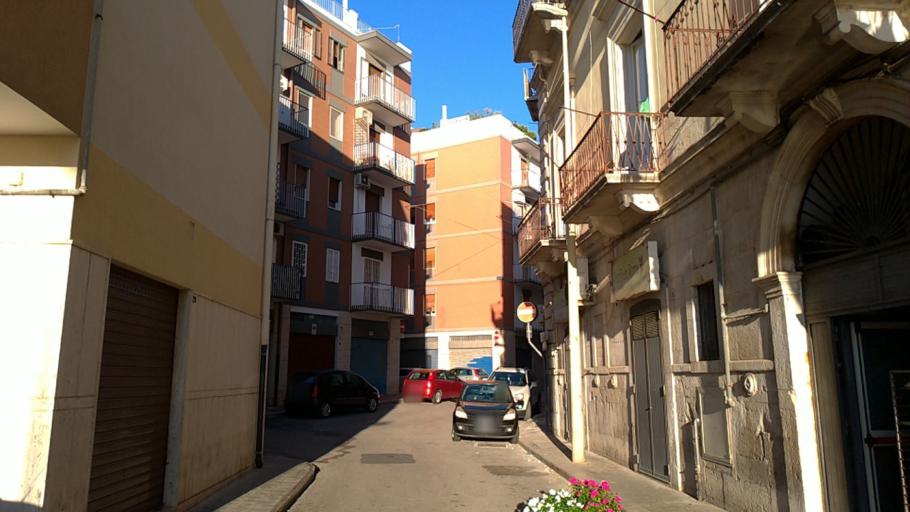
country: IT
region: Apulia
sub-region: Provincia di Bari
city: Giovinazzo
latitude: 41.1873
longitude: 16.6745
